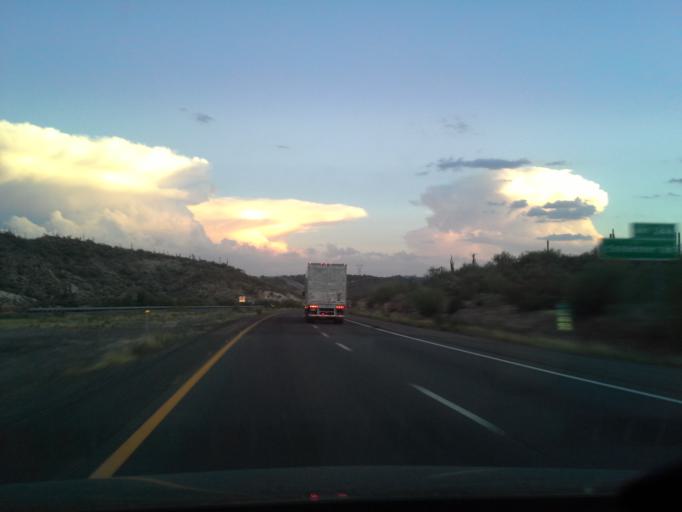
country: US
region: Arizona
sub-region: Yavapai County
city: Black Canyon City
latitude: 34.0938
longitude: -112.1429
